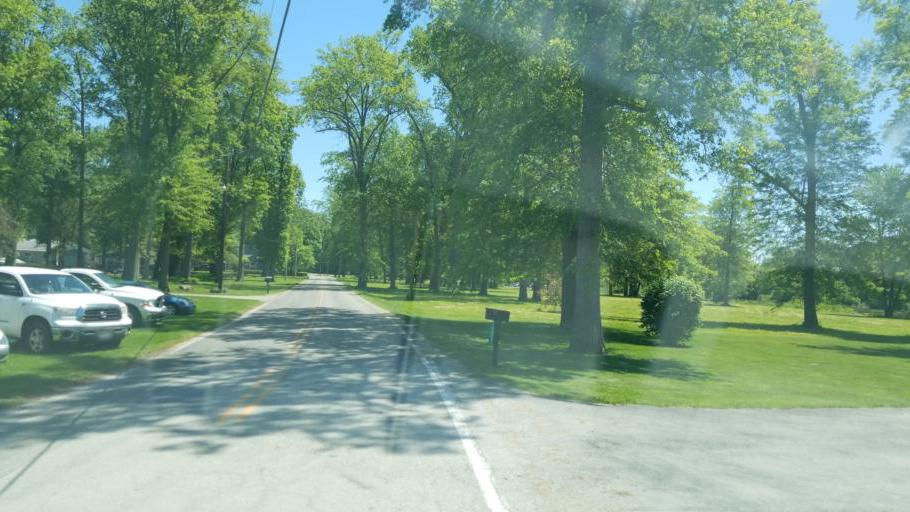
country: US
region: Ohio
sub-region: Shelby County
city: Fort Loramie
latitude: 40.3695
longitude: -84.3416
